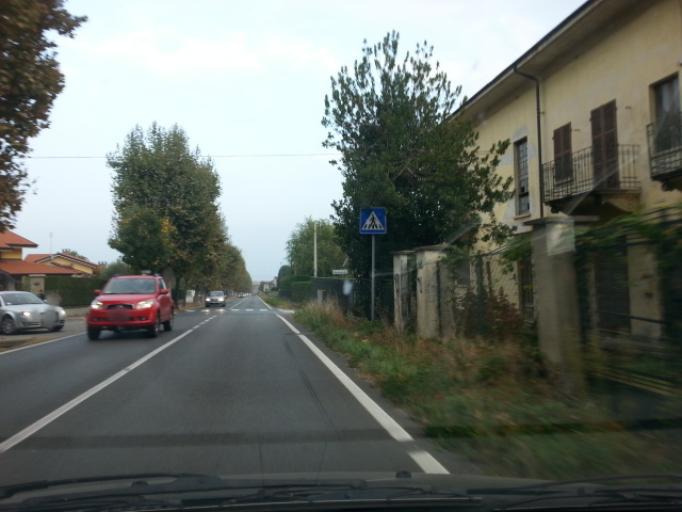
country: IT
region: Piedmont
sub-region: Provincia di Torino
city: Giaveno
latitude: 45.0412
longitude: 7.3374
